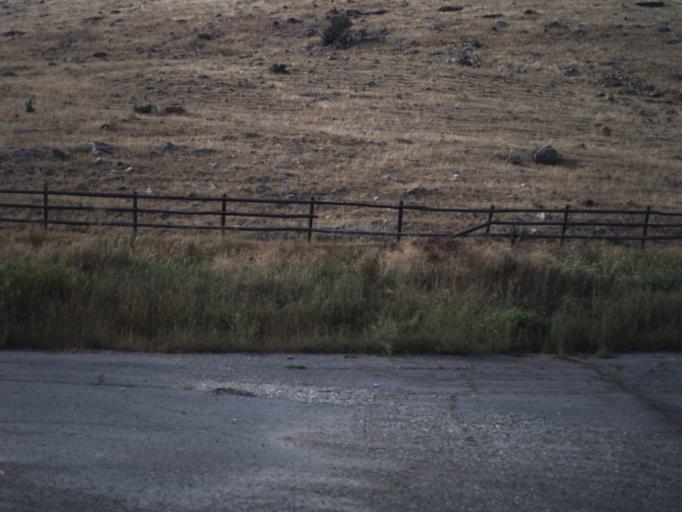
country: US
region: Utah
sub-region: Cache County
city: Millville
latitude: 41.6022
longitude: -111.5669
